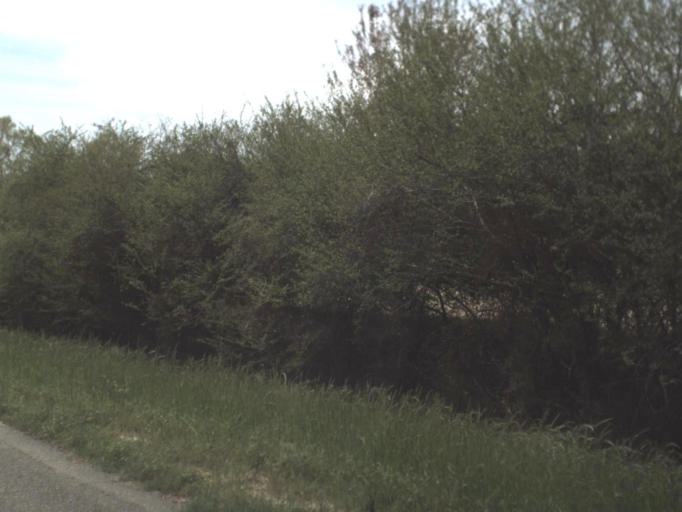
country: US
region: Florida
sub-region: Washington County
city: Chipley
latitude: 30.8459
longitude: -85.5302
